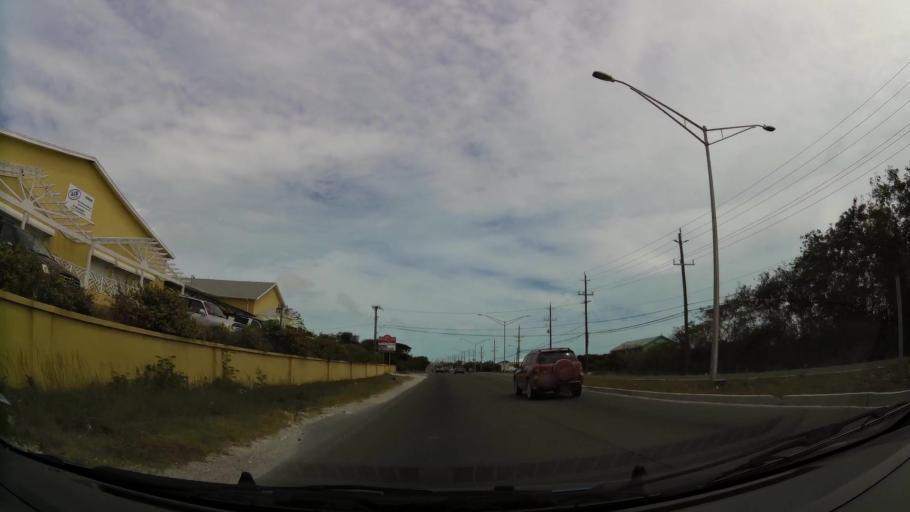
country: BS
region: Mayaguana
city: Abraham's Bay
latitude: 21.7802
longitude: -72.2378
